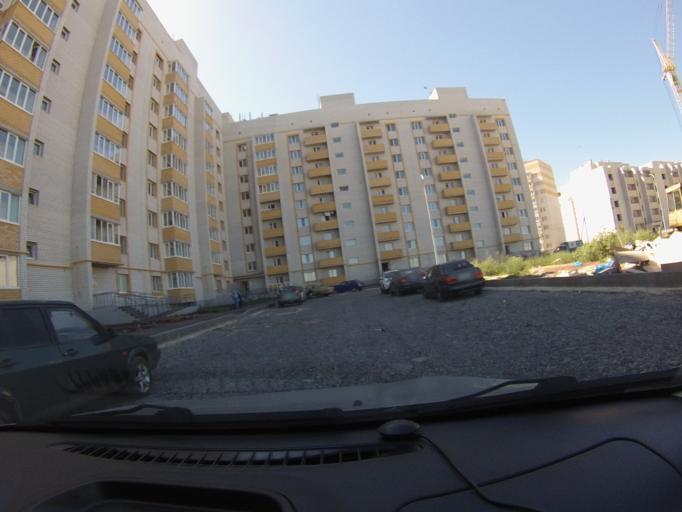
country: RU
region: Tambov
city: Tambov
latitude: 52.7761
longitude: 41.4135
